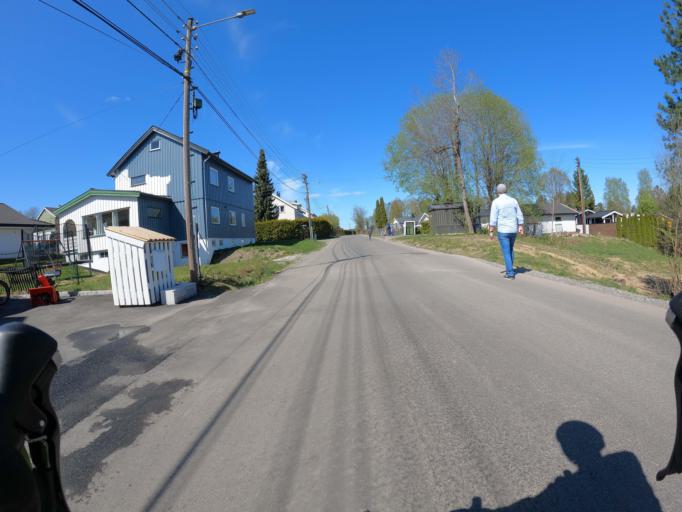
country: NO
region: Akershus
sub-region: Skedsmo
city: Leirsund
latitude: 60.0045
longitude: 11.0437
